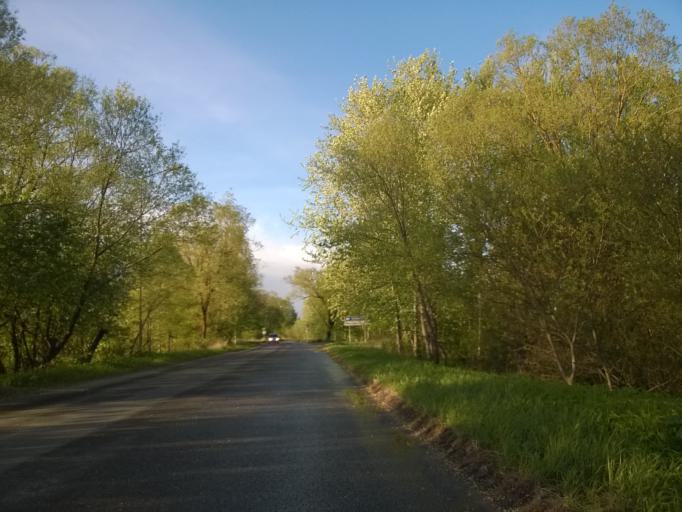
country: LV
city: Tireli
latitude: 56.9330
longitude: 23.6059
